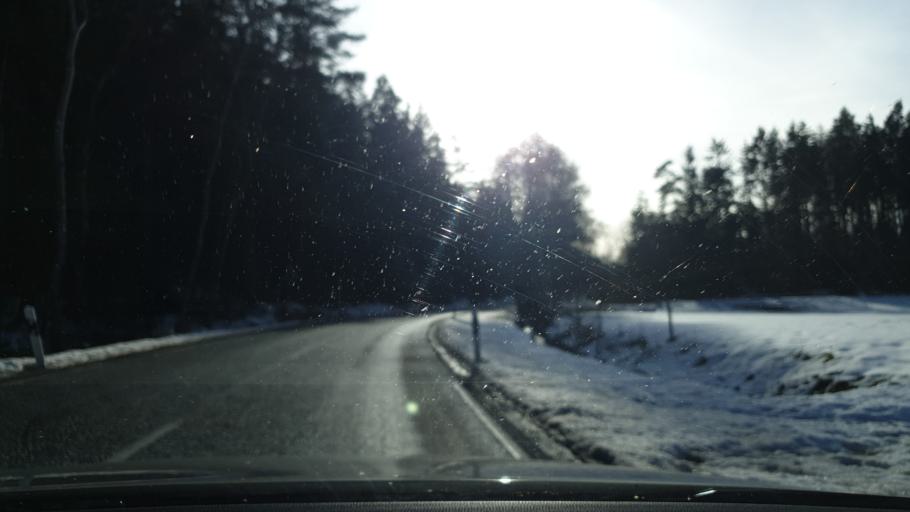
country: DE
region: Thuringia
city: Kauern
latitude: 50.7242
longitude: 12.0669
